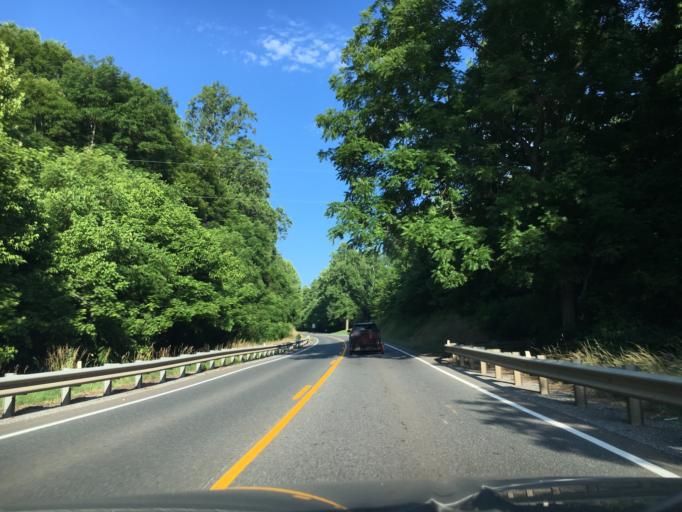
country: US
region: Virginia
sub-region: Bedford County
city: Forest
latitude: 37.3723
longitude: -79.3194
